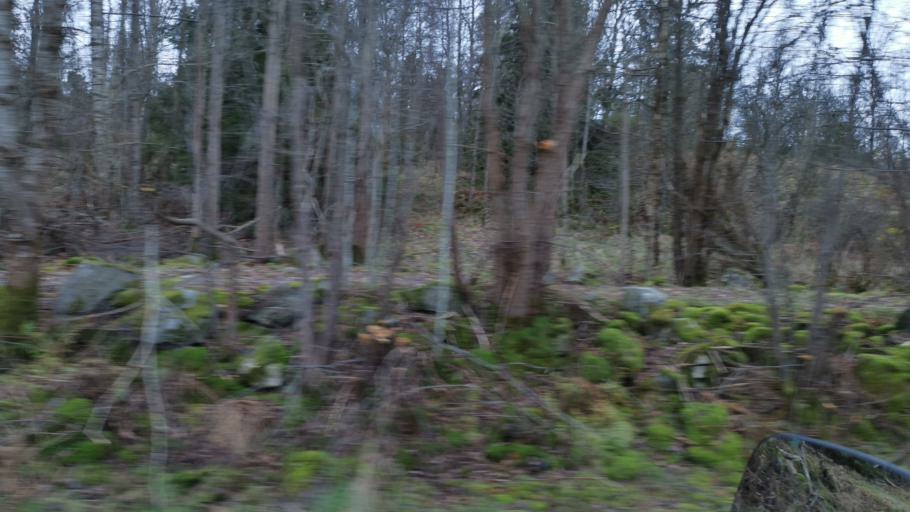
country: SE
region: Vaestra Goetaland
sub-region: Orust
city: Henan
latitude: 58.2242
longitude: 11.7035
